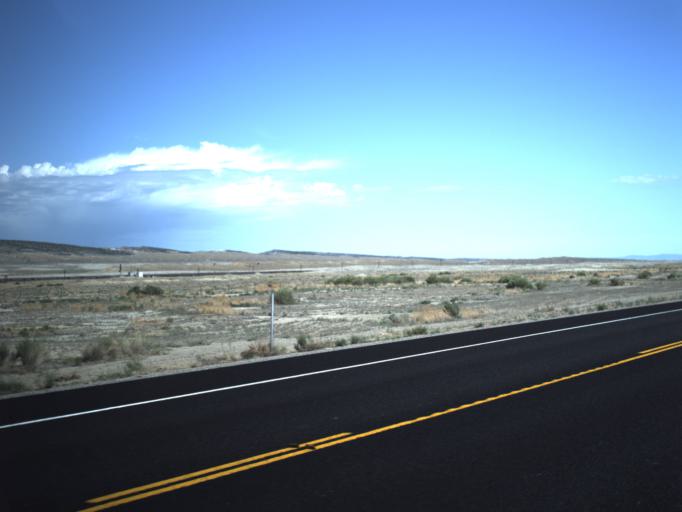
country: US
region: Utah
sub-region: Carbon County
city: East Carbon City
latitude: 39.1679
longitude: -110.3382
